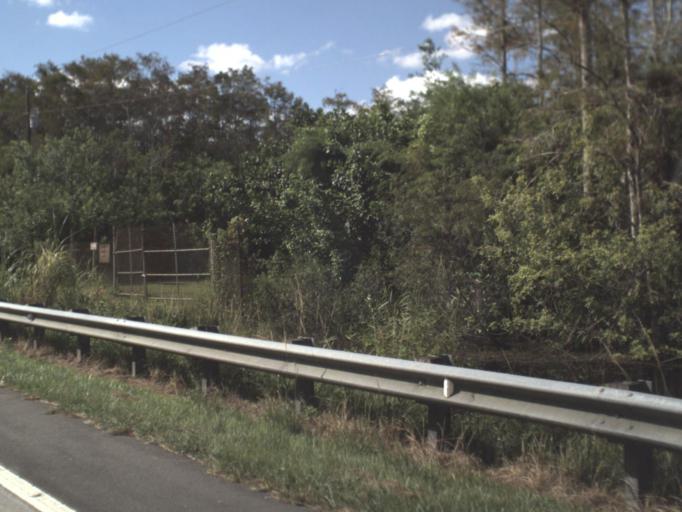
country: US
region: Florida
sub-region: Miami-Dade County
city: Kendall West
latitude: 25.8561
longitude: -81.0256
